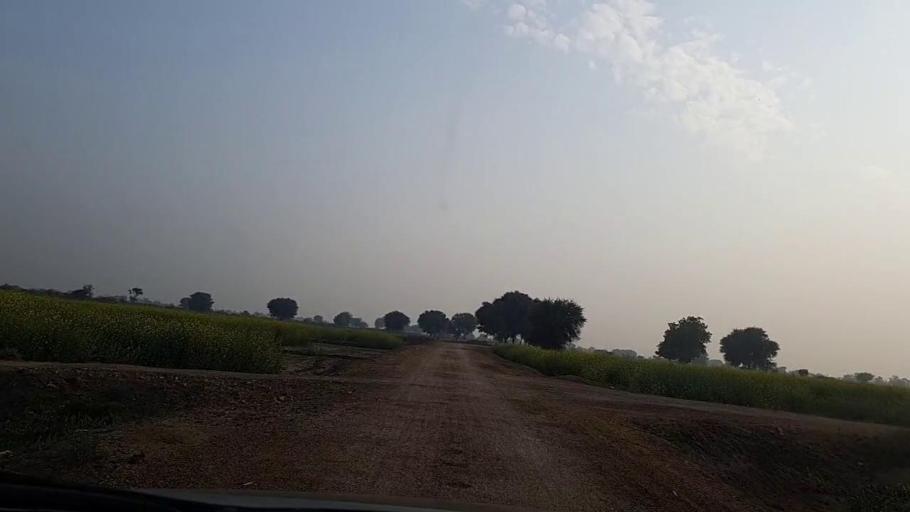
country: PK
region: Sindh
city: Nawabshah
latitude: 26.2707
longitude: 68.3235
